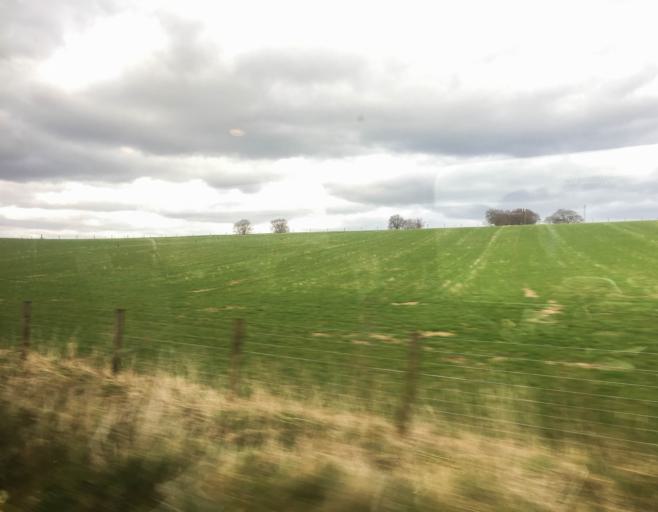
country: GB
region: Scotland
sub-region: South Lanarkshire
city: Carnwath
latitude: 55.6501
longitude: -3.6342
